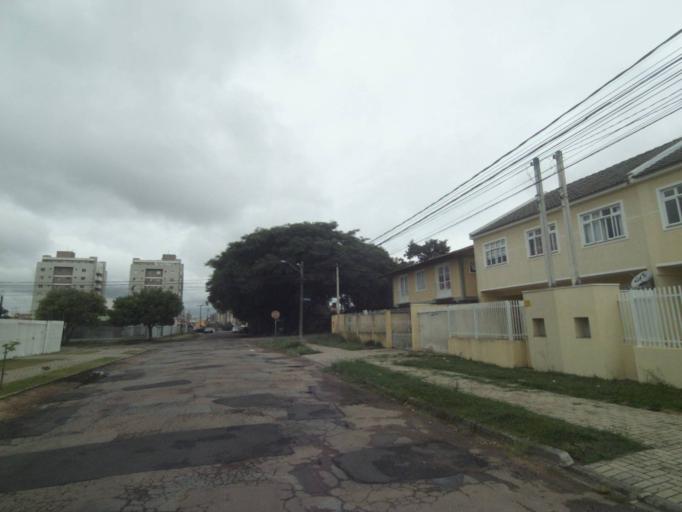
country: BR
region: Parana
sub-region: Curitiba
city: Curitiba
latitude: -25.4955
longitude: -49.3060
